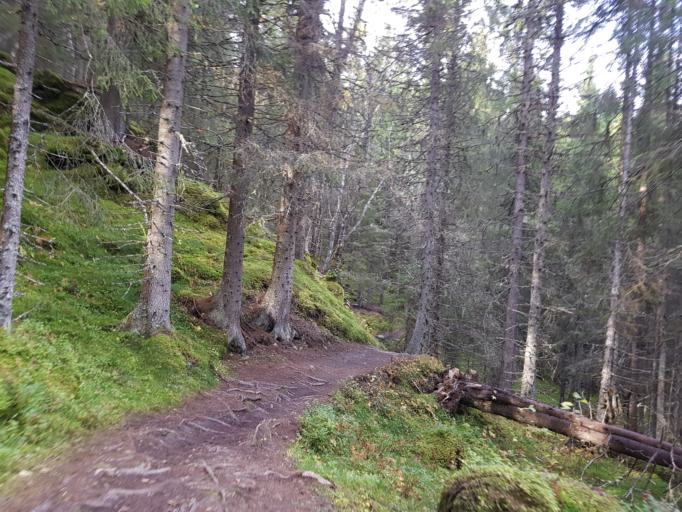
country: NO
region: Sor-Trondelag
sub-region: Trondheim
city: Trondheim
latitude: 63.4491
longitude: 10.2700
